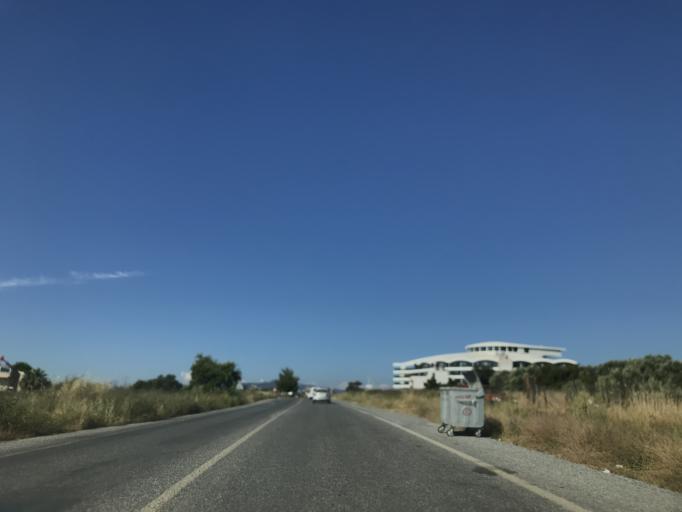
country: TR
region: Aydin
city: Davutlar
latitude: 37.7260
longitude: 27.2621
